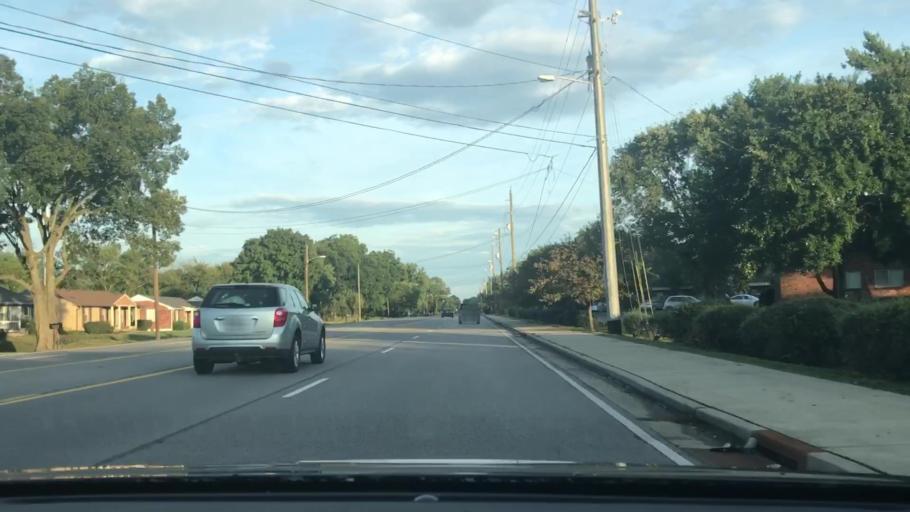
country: US
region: Tennessee
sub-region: Davidson County
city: Oak Hill
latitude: 36.0808
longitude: -86.7514
